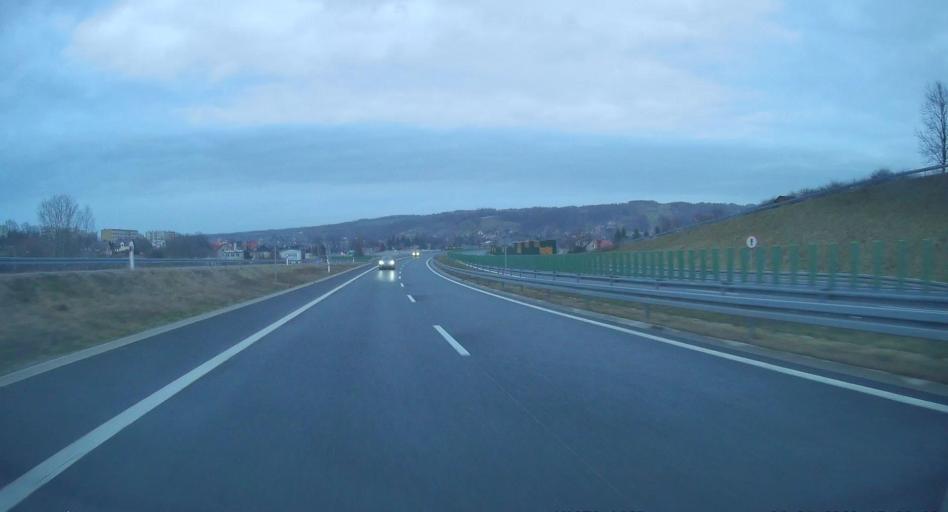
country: PL
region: Subcarpathian Voivodeship
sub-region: Powiat ropczycko-sedziszowski
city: Ropczyce
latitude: 50.0569
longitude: 21.5946
